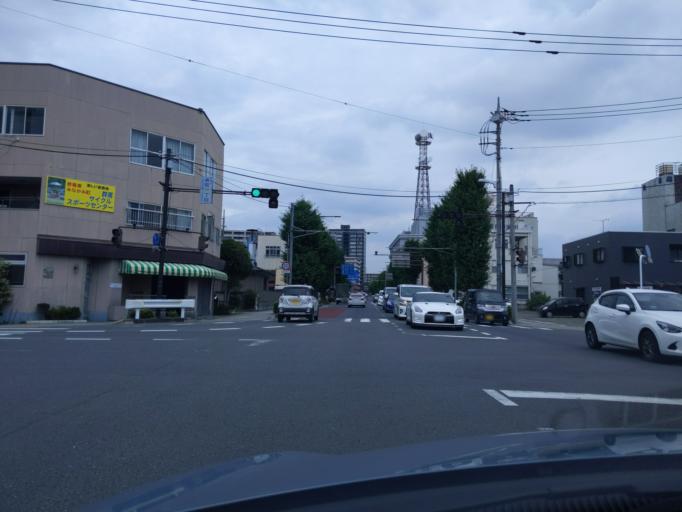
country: JP
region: Gunma
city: Maebashi-shi
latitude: 36.3878
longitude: 139.0676
